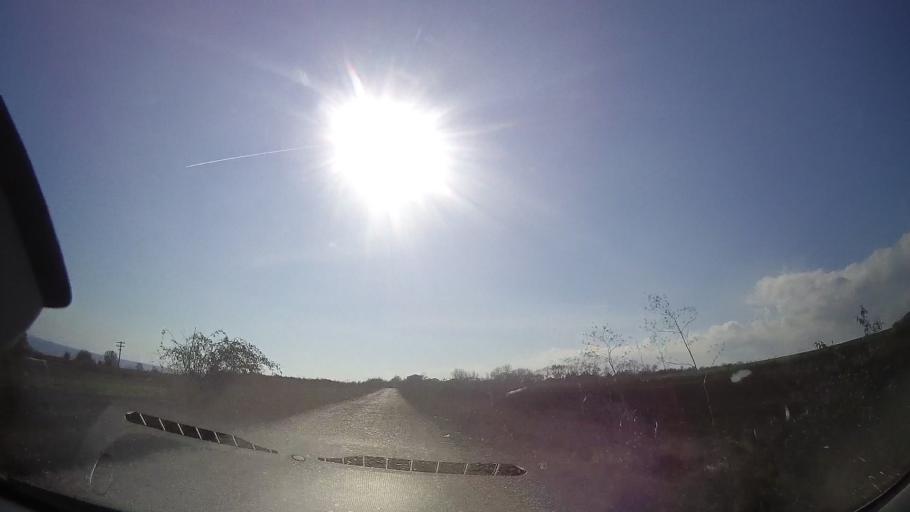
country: RO
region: Constanta
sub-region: Comuna Douazeci si Trei August
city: Douazeci si Trei August
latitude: 43.9065
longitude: 28.6191
